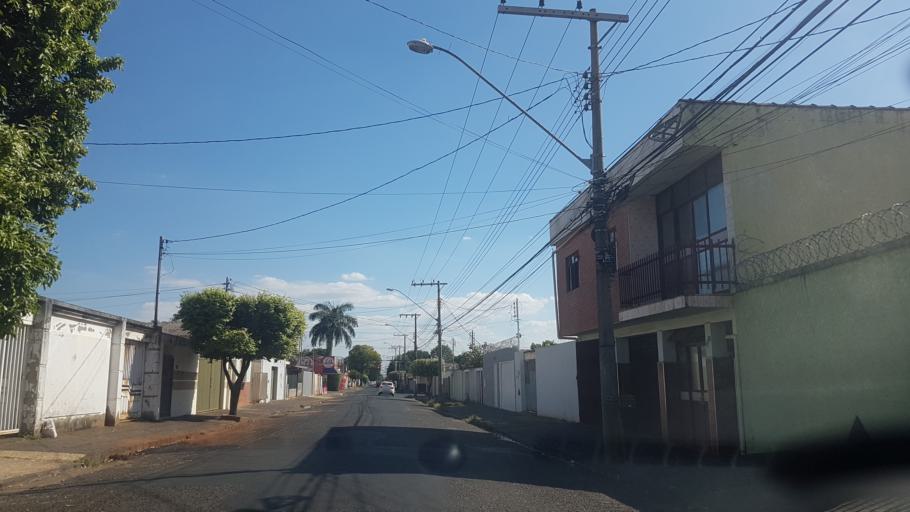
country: BR
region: Minas Gerais
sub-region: Uberlandia
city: Uberlandia
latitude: -18.9080
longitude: -48.2860
